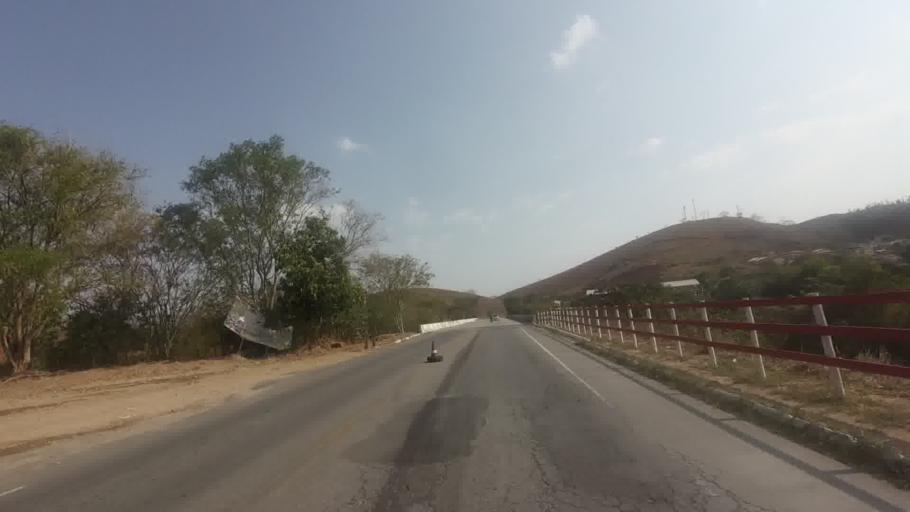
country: BR
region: Rio de Janeiro
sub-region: Bom Jesus Do Itabapoana
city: Bom Jesus do Itabapoana
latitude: -21.1333
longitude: -41.6606
